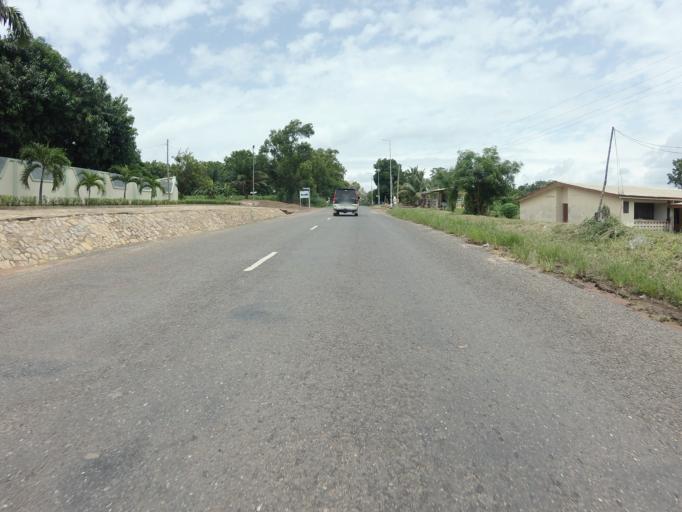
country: GH
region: Volta
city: Ho
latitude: 6.5970
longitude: 0.4629
